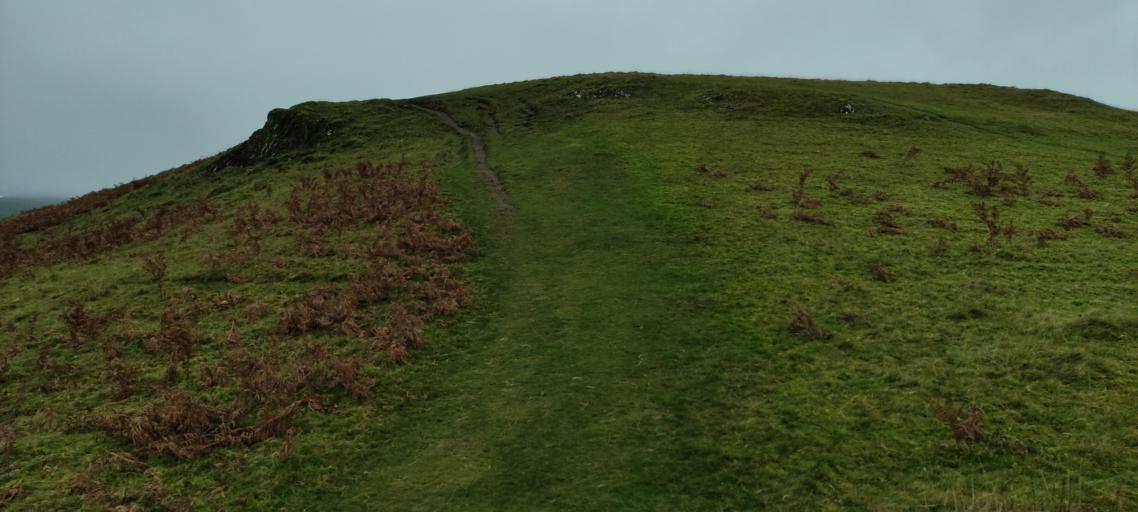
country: GB
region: England
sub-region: Cumbria
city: Cockermouth
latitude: 54.6542
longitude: -3.2428
